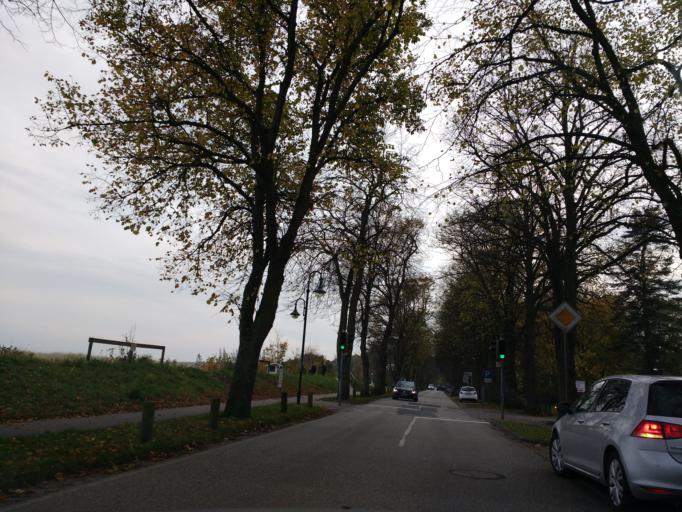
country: DE
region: Mecklenburg-Vorpommern
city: Ostseebad Boltenhagen
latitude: 53.9931
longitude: 11.1983
